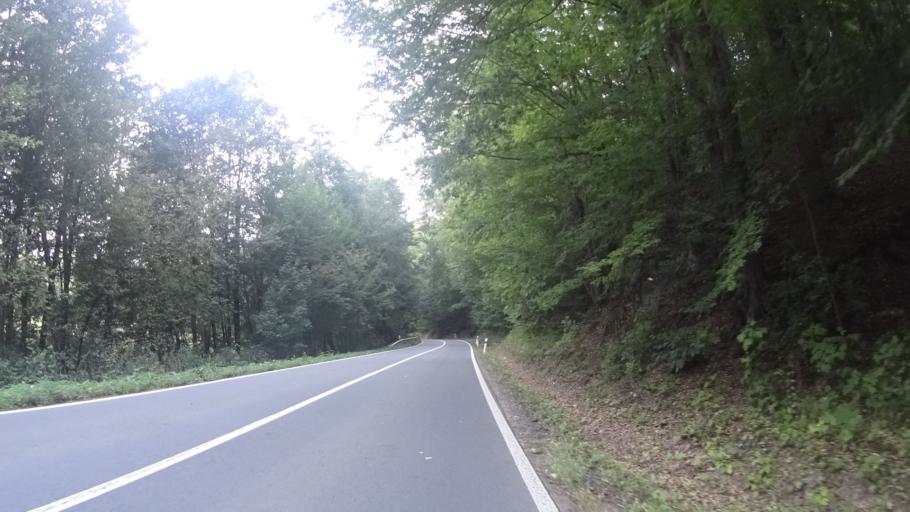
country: CZ
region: Olomoucky
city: Stity
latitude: 49.8653
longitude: 16.7371
